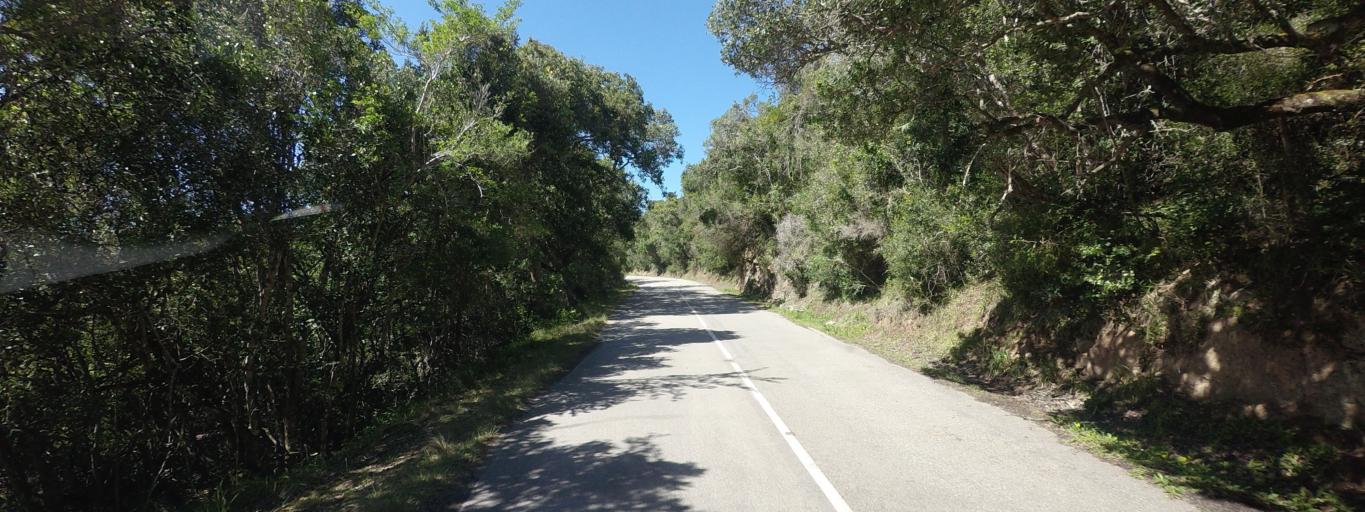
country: ZA
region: Western Cape
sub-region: Eden District Municipality
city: Plettenberg Bay
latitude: -33.9719
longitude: 23.5617
